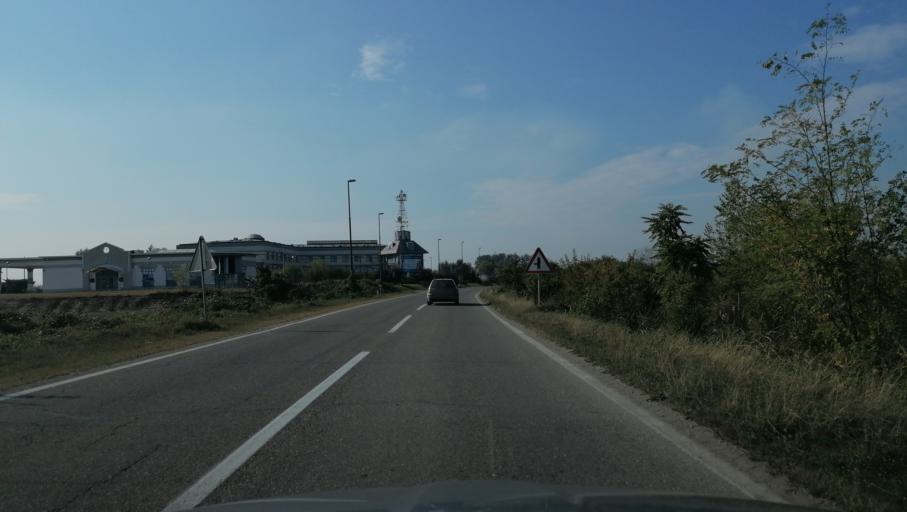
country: BA
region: Republika Srpska
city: Popovi
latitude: 44.7784
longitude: 19.3210
